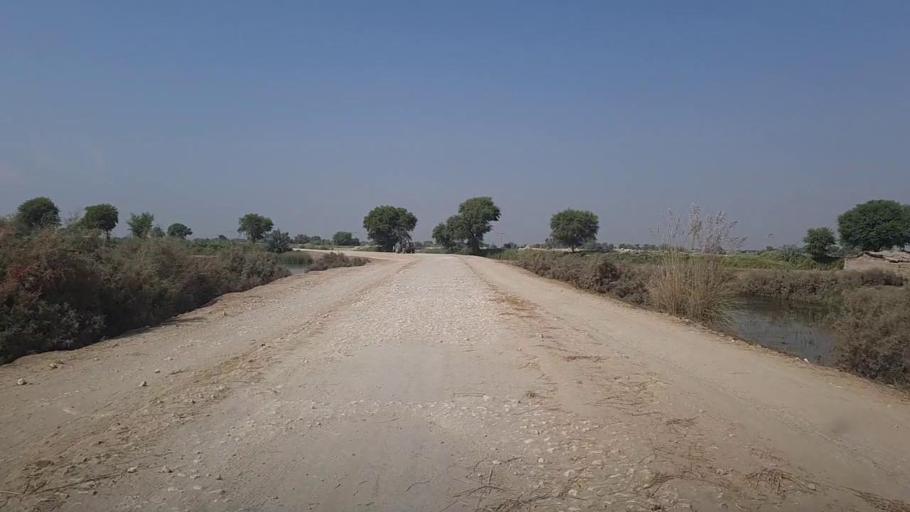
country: PK
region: Sindh
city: Kandhkot
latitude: 28.3894
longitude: 69.3370
